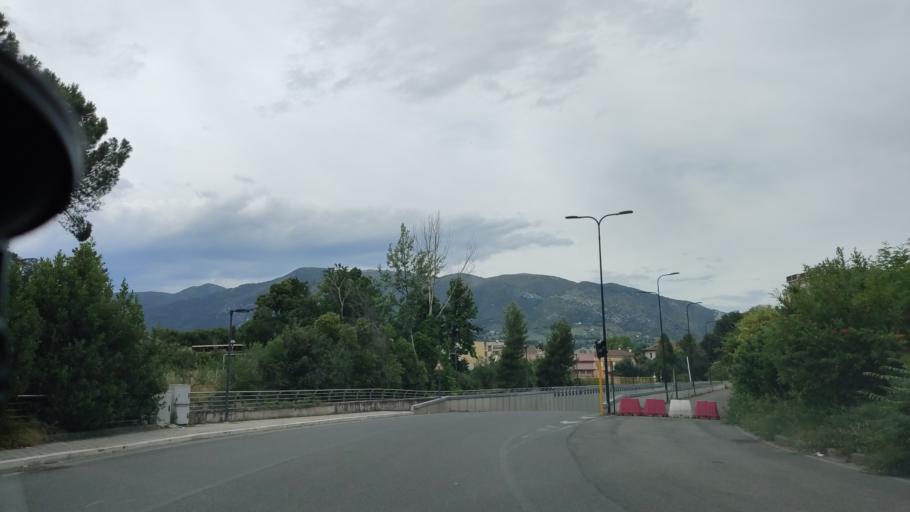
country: IT
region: Umbria
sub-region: Provincia di Terni
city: Terni
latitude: 42.5656
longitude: 12.6590
